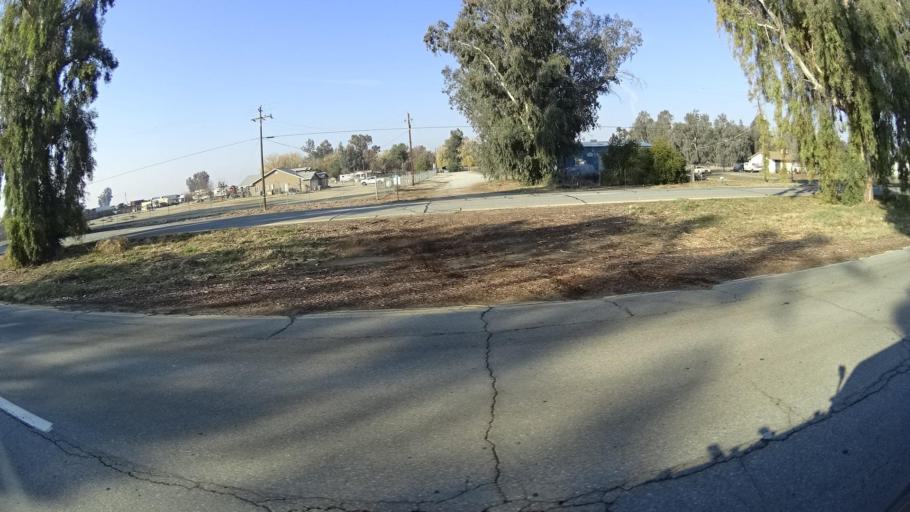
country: US
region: California
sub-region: Kern County
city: Greenfield
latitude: 35.1949
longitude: -119.0030
